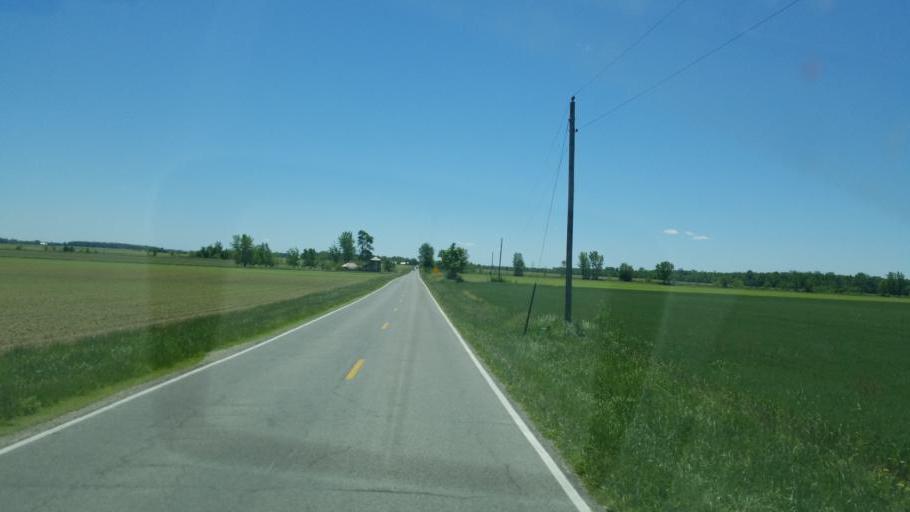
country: US
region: Indiana
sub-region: Randolph County
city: Union City
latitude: 40.2977
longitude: -84.8038
